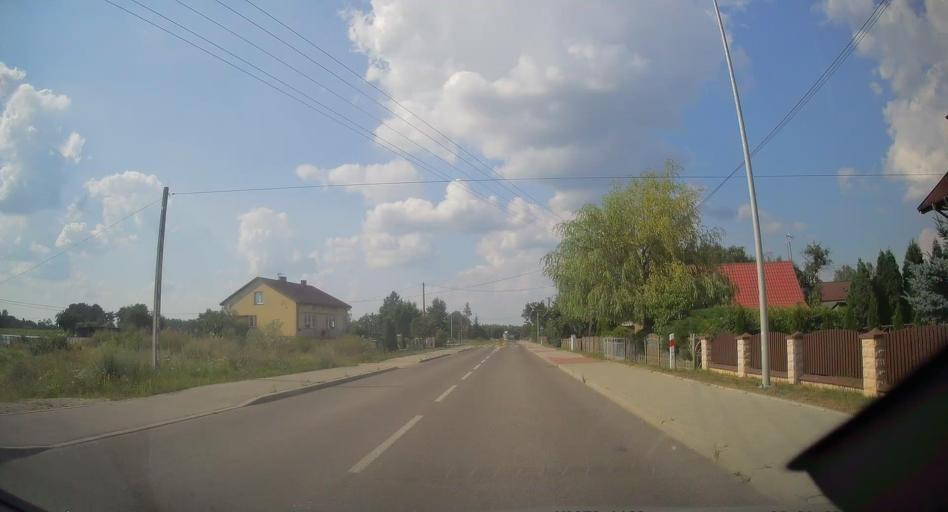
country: PL
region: Swietokrzyskie
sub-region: Powiat konecki
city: Radoszyce
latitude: 51.0518
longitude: 20.2810
